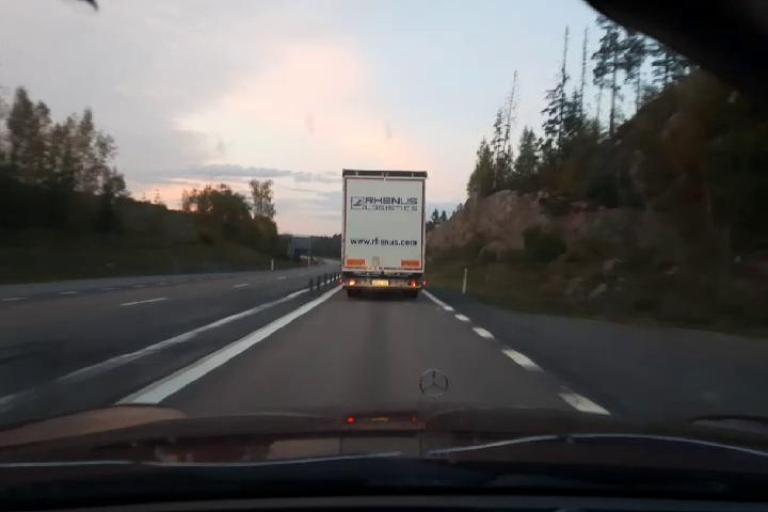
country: SE
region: Vaesternorrland
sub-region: Haernoesands Kommun
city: Haernoesand
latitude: 62.8177
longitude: 17.9690
